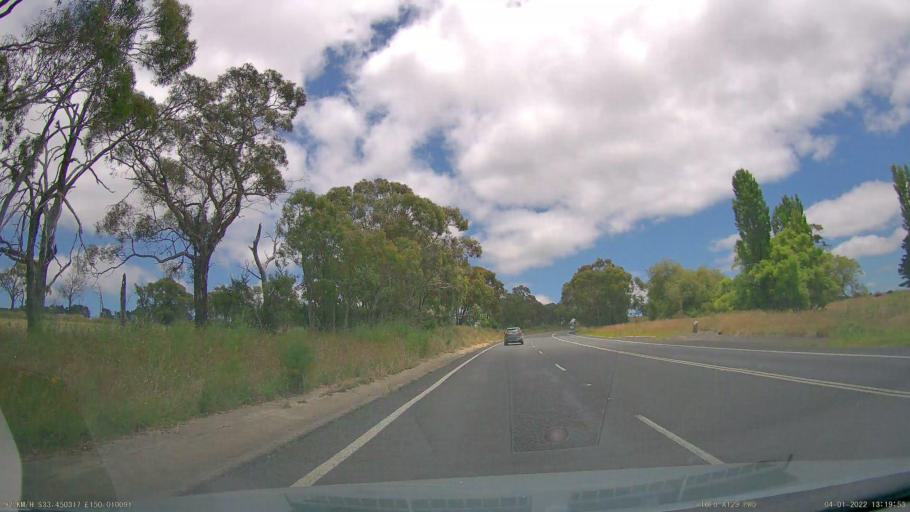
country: AU
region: New South Wales
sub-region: Lithgow
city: Portland
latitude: -33.4503
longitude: 150.0095
